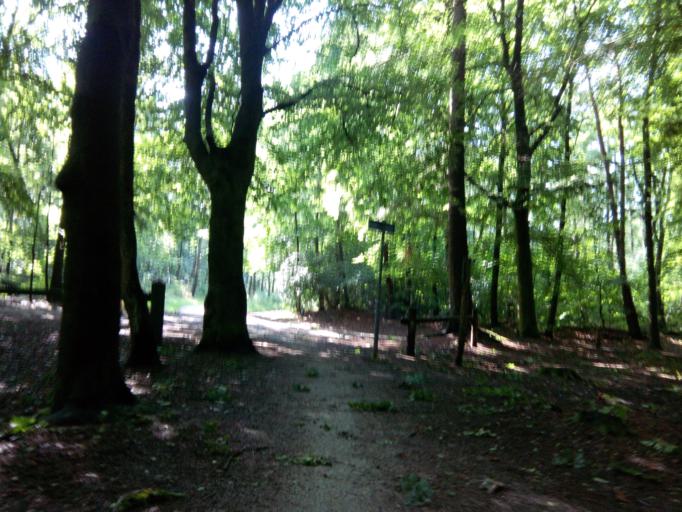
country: NL
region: Utrecht
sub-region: Gemeente Utrechtse Heuvelrug
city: Doorn
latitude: 52.0503
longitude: 5.3331
